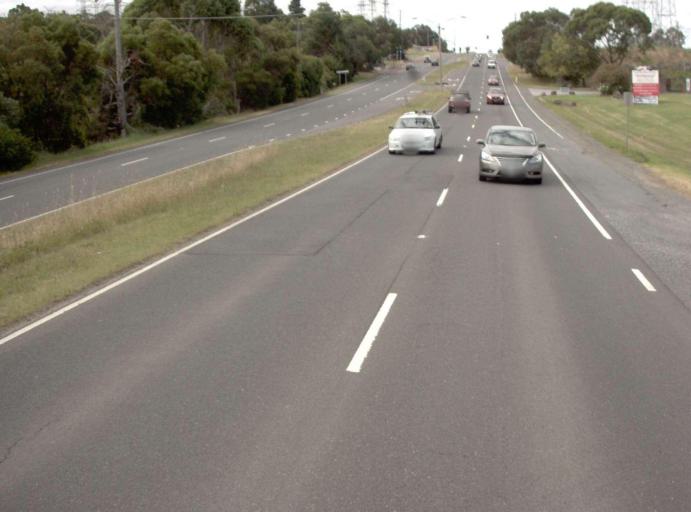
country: AU
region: Victoria
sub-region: Knox
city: Rowville
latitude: -37.9388
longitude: 145.2312
